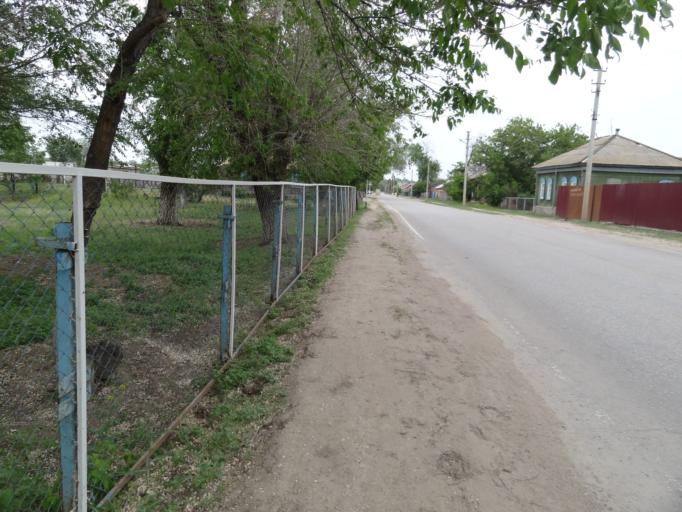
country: RU
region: Saratov
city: Privolzhskiy
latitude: 51.1852
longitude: 45.9175
